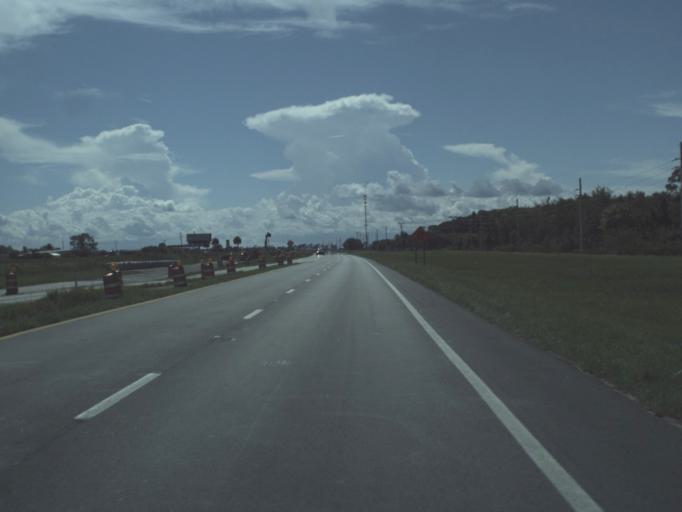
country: US
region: Florida
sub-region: Okeechobee County
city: Taylor Creek
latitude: 27.2935
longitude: -80.6938
